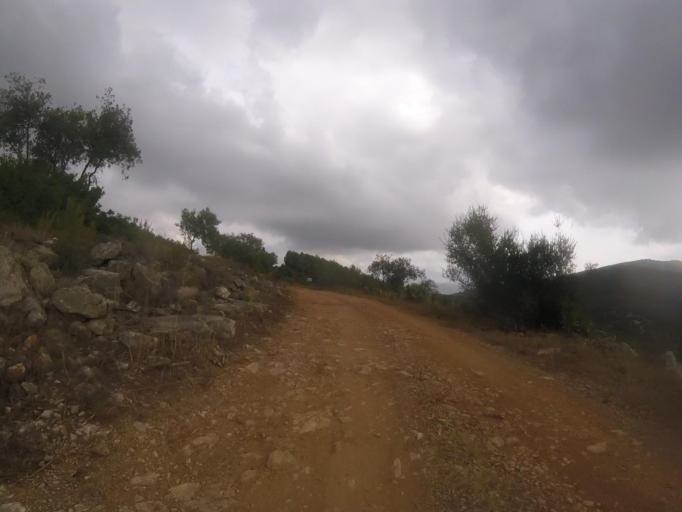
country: ES
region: Valencia
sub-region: Provincia de Castello
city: Santa Magdalena de Pulpis
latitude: 40.3268
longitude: 0.2887
